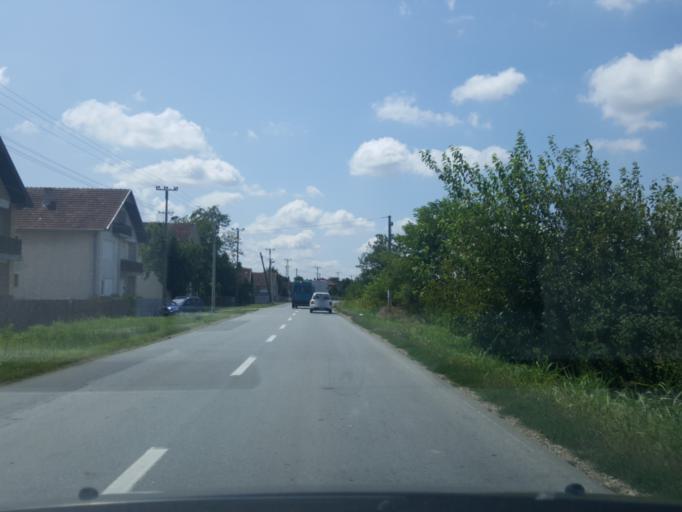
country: RS
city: Salas Nocajski
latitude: 44.9406
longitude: 19.5756
